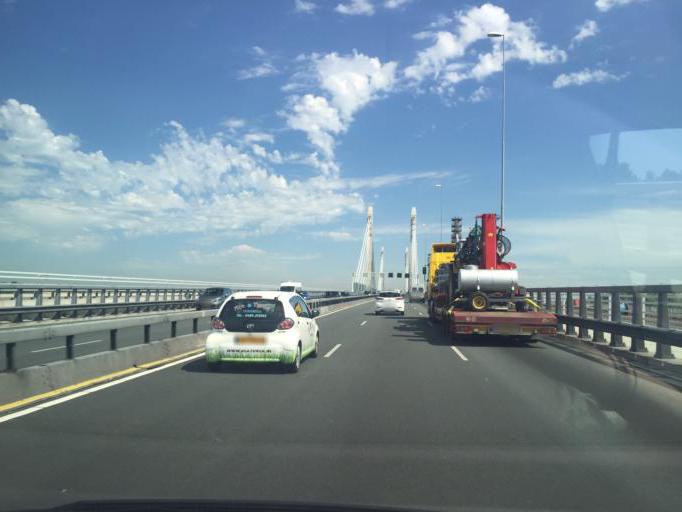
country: NL
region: Gelderland
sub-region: Gemeente Overbetuwe
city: Andelst
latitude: 51.8812
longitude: 5.7356
